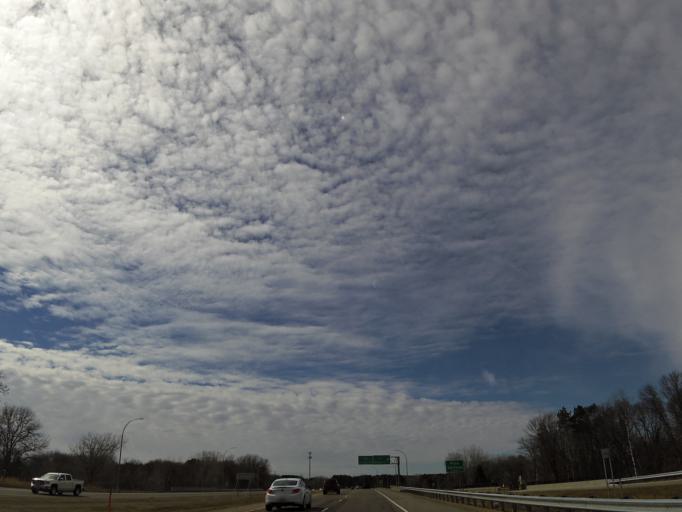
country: US
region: Minnesota
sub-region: Washington County
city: Mahtomedi
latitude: 45.0361
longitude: -92.9441
